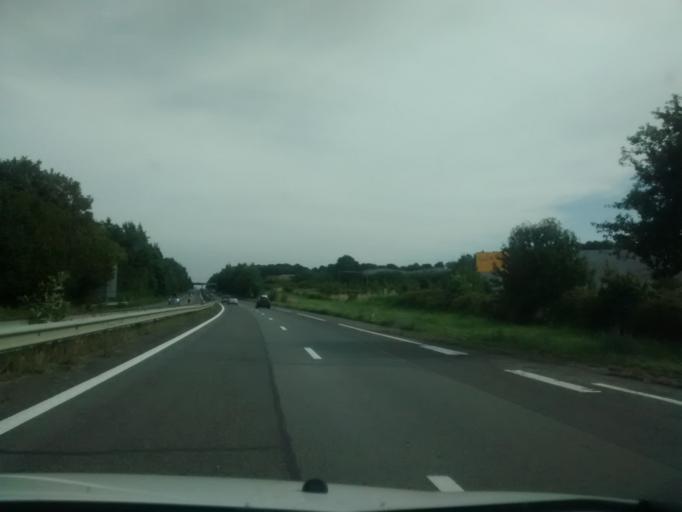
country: FR
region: Brittany
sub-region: Departement d'Ille-et-Vilaine
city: Miniac-Morvan
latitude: 48.5297
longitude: -1.9187
